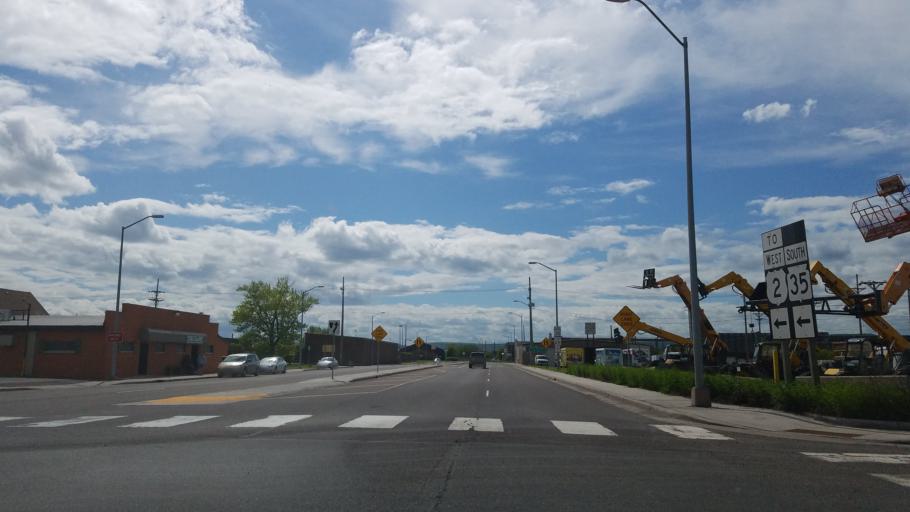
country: US
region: Wisconsin
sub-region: Douglas County
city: Superior
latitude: 46.7353
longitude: -92.0993
